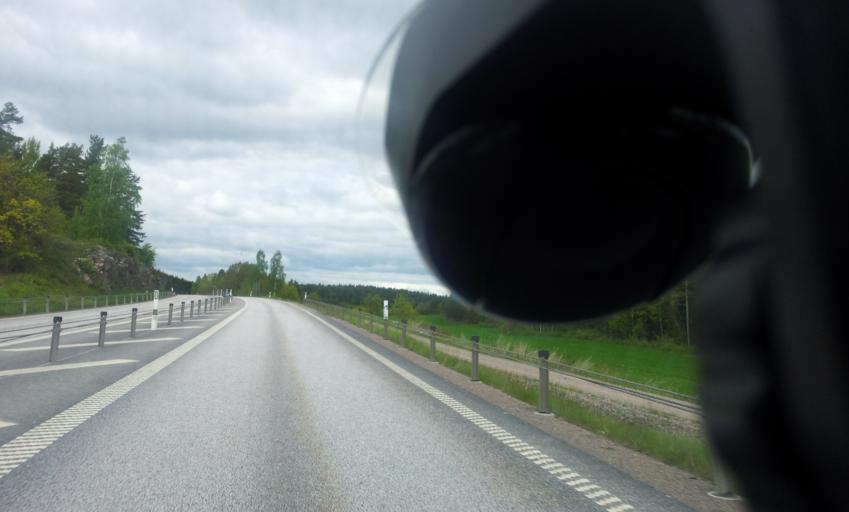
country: SE
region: Kalmar
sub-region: Vasterviks Kommun
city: Gamleby
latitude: 57.9195
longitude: 16.3998
